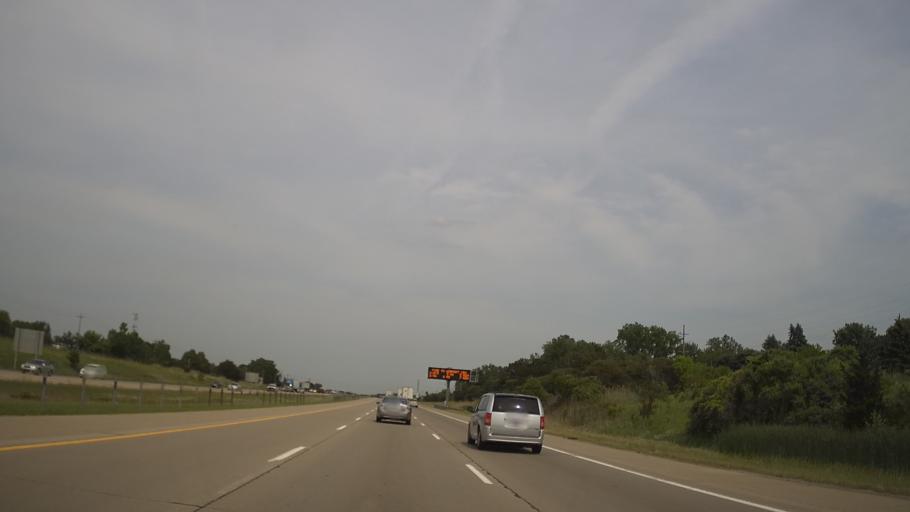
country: US
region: Michigan
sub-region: Wayne County
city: Belleville
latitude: 42.2198
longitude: -83.4739
